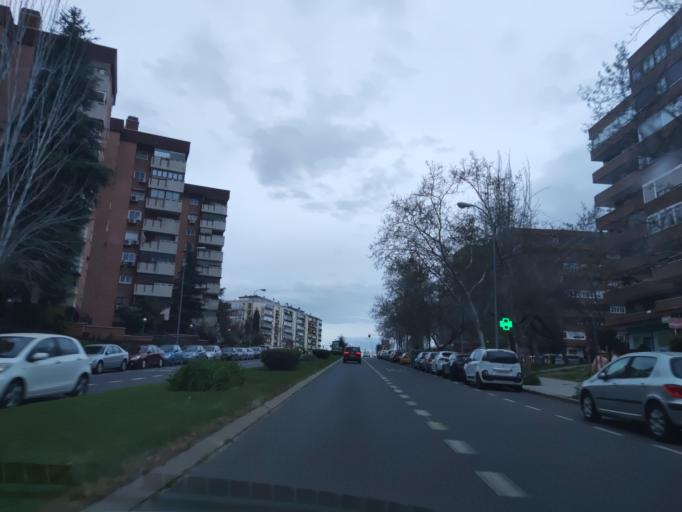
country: ES
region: Madrid
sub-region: Provincia de Madrid
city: Hortaleza
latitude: 40.4665
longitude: -3.6366
